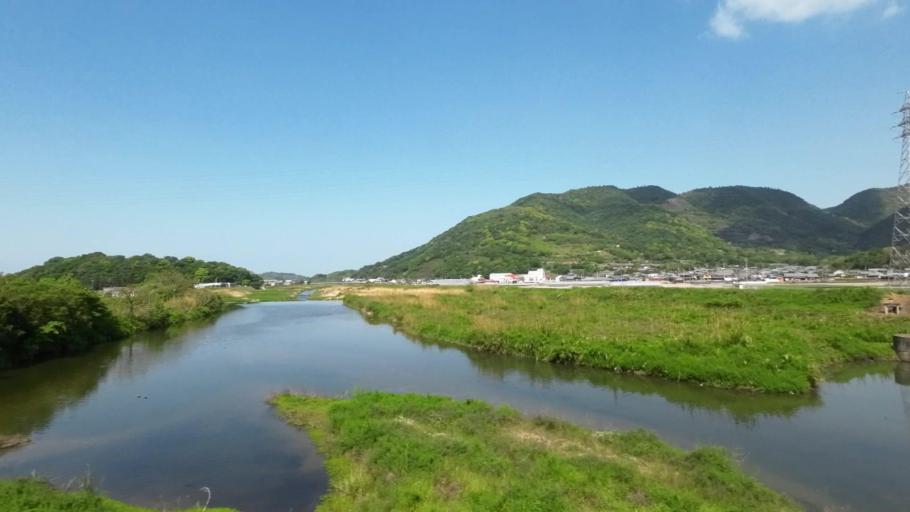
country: JP
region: Kagawa
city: Kan'onjicho
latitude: 34.1391
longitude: 133.6849
